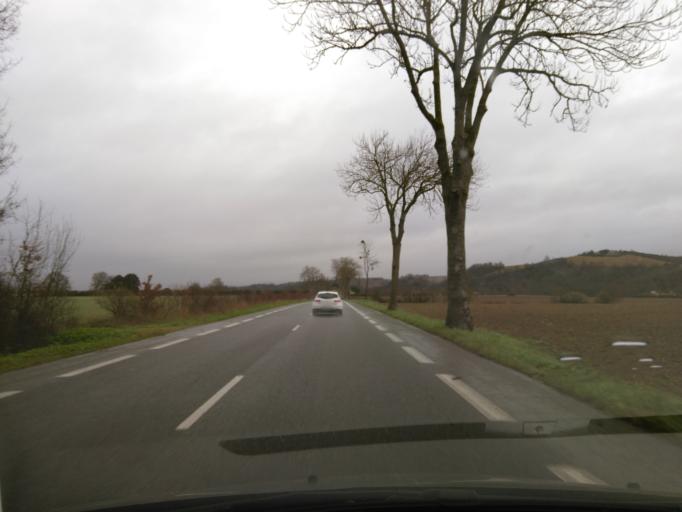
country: FR
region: Midi-Pyrenees
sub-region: Departement de la Haute-Garonne
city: Rieux-Volvestre
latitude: 43.2764
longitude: 1.2063
